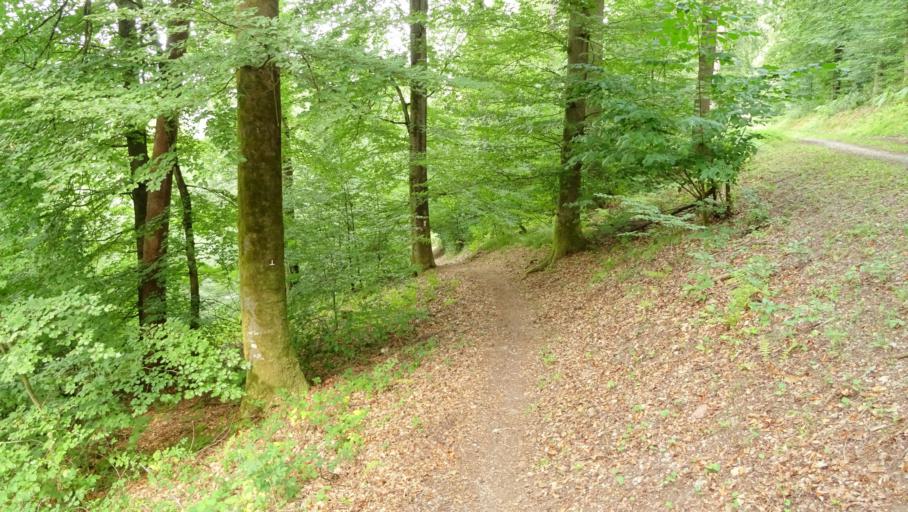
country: DE
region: Baden-Wuerttemberg
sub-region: Karlsruhe Region
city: Neckargerach
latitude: 49.4044
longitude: 9.0907
